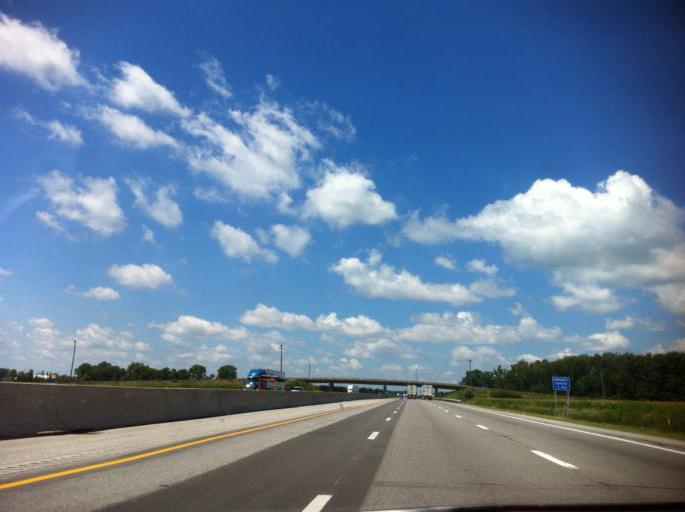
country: US
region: Ohio
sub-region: Ottawa County
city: Elmore
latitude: 41.4406
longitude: -83.2371
